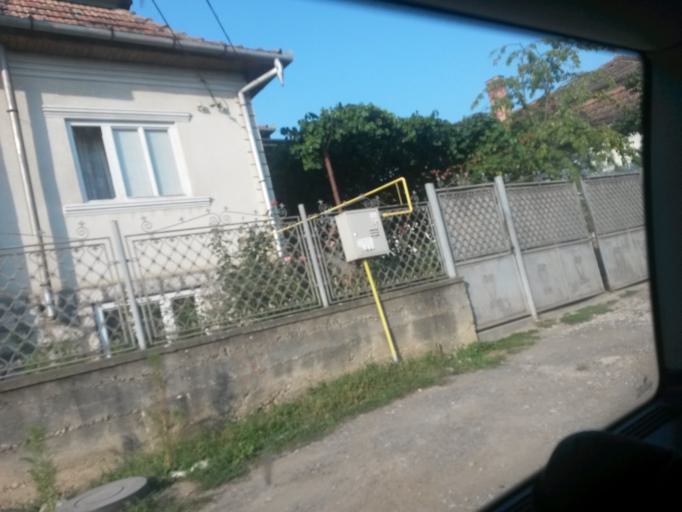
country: RO
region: Alba
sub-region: Municipiul Aiud
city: Aiudul de Sus
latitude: 46.3193
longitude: 23.6863
